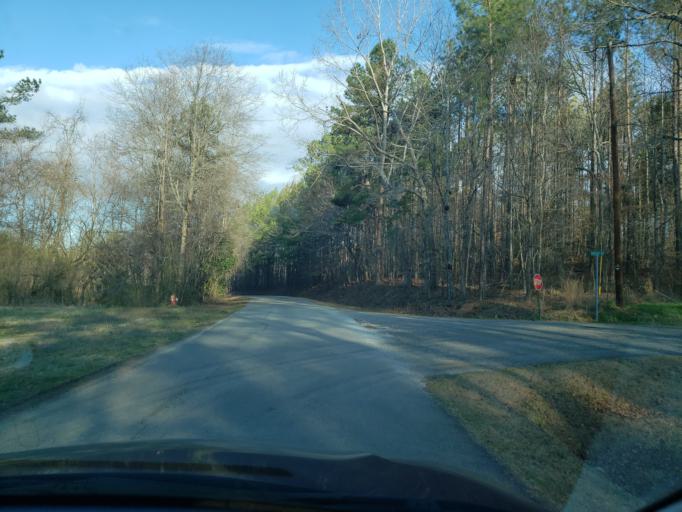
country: US
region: Alabama
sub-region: Cleburne County
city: Heflin
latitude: 33.6343
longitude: -85.5970
